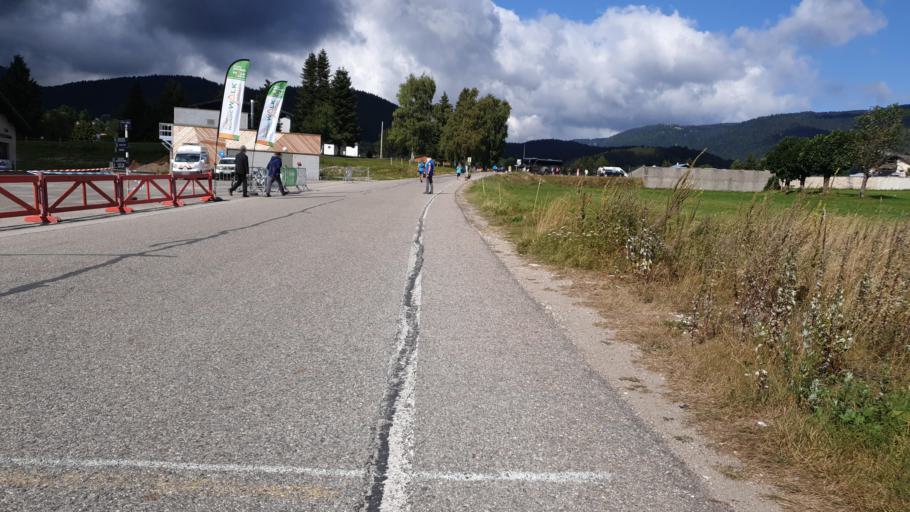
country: FR
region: Rhone-Alpes
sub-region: Departement de l'Isere
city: Autrans
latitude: 45.1763
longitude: 5.5401
